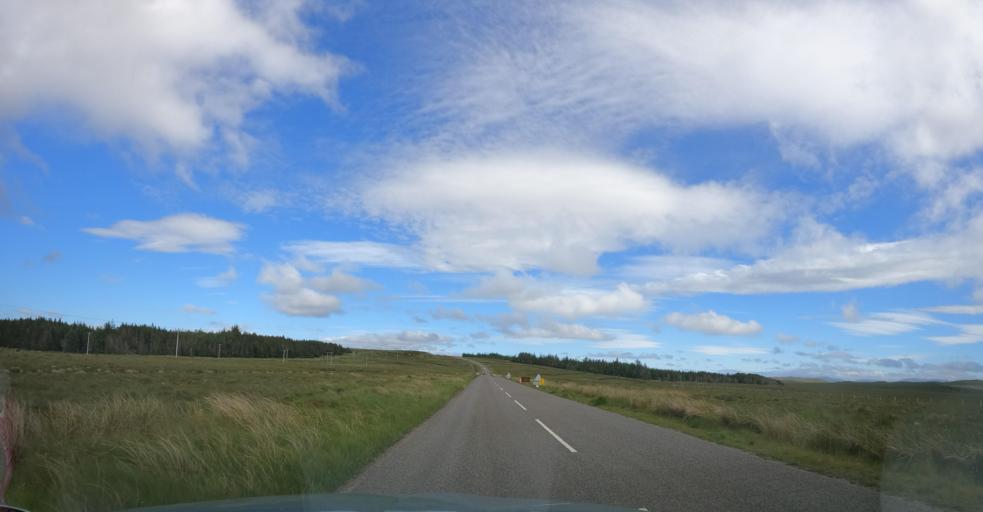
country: GB
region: Scotland
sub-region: Eilean Siar
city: Isle of Lewis
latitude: 58.1827
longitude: -6.6679
